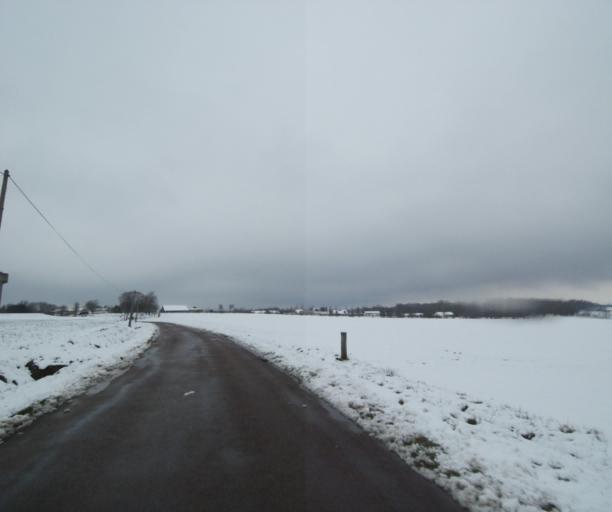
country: FR
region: Champagne-Ardenne
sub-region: Departement de la Haute-Marne
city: Laneuville-a-Remy
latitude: 48.5069
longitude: 4.8510
